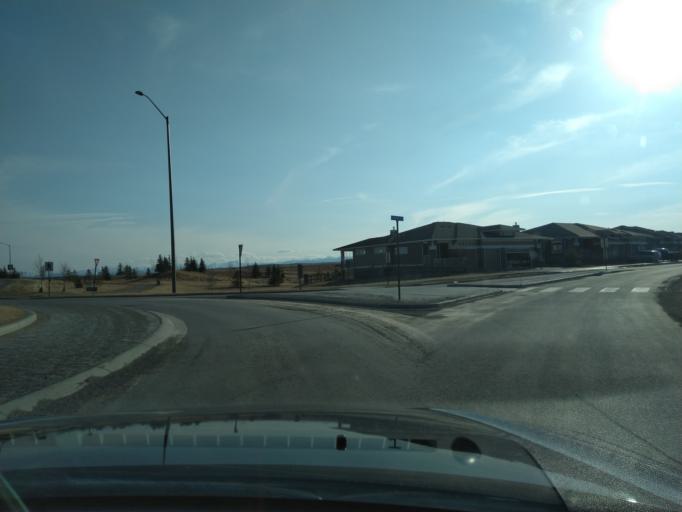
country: CA
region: Alberta
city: Cochrane
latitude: 51.1093
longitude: -114.3912
